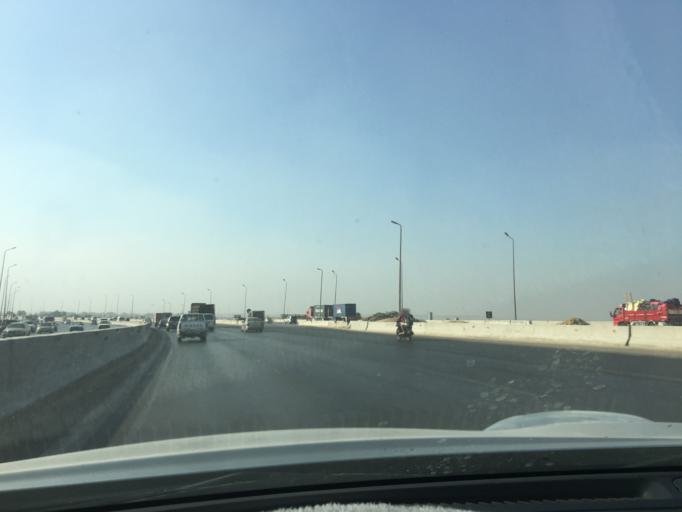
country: EG
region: Muhafazat al Qalyubiyah
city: Al Khankah
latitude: 30.1285
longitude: 31.4649
